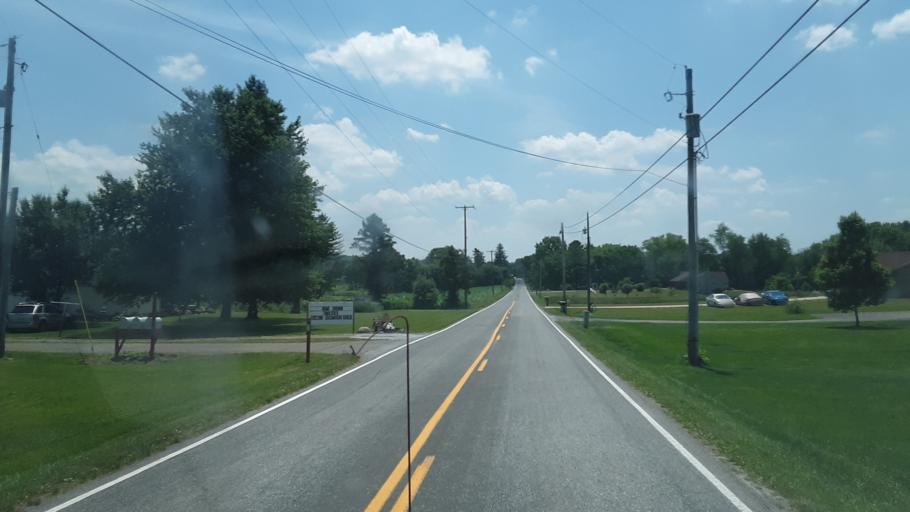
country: US
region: Ohio
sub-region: Stark County
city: Brewster
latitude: 40.6863
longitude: -81.5799
